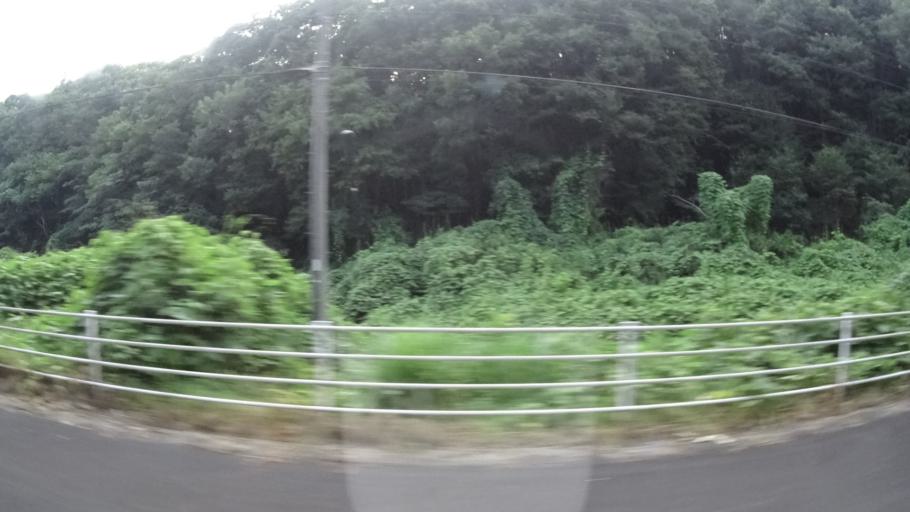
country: JP
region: Tochigi
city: Karasuyama
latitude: 36.6149
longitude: 140.1554
